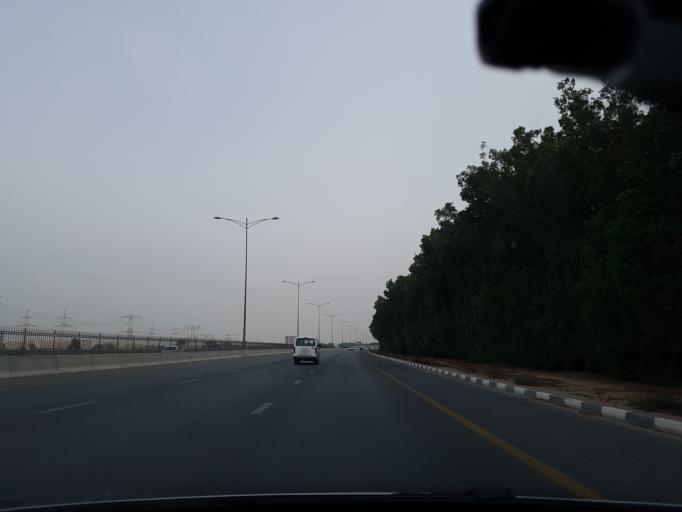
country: AE
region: Ajman
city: Ajman
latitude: 25.3639
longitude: 55.4727
